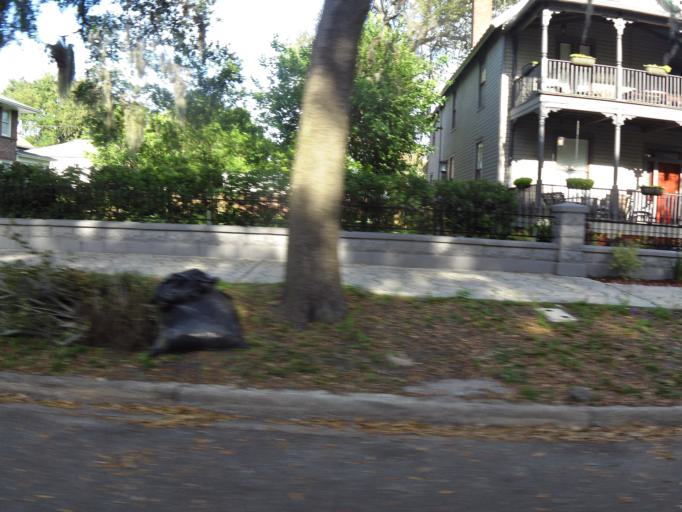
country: US
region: Florida
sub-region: Duval County
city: Jacksonville
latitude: 30.3384
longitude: -81.6563
